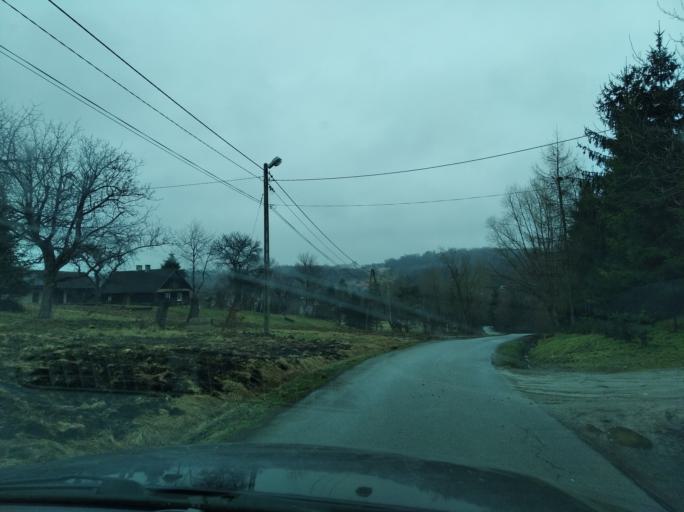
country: PL
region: Subcarpathian Voivodeship
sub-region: Powiat rzeszowski
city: Tyczyn
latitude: 49.9465
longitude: 22.0211
